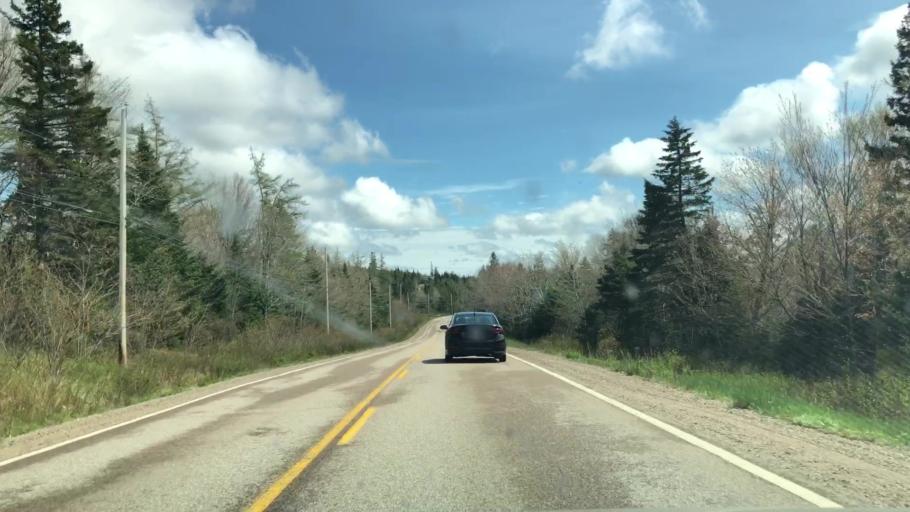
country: CA
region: Nova Scotia
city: Antigonish
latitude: 45.2126
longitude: -62.0051
